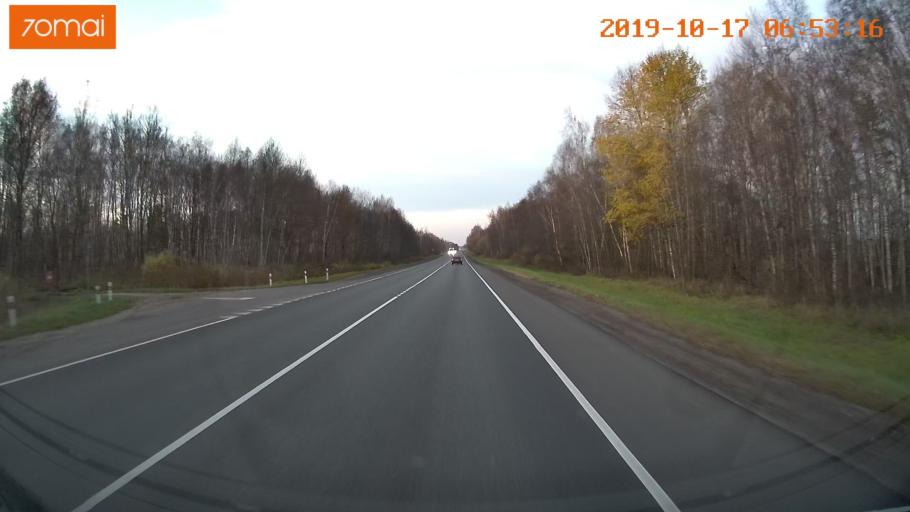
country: RU
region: Vladimir
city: Kideksha
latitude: 56.4766
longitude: 40.4902
